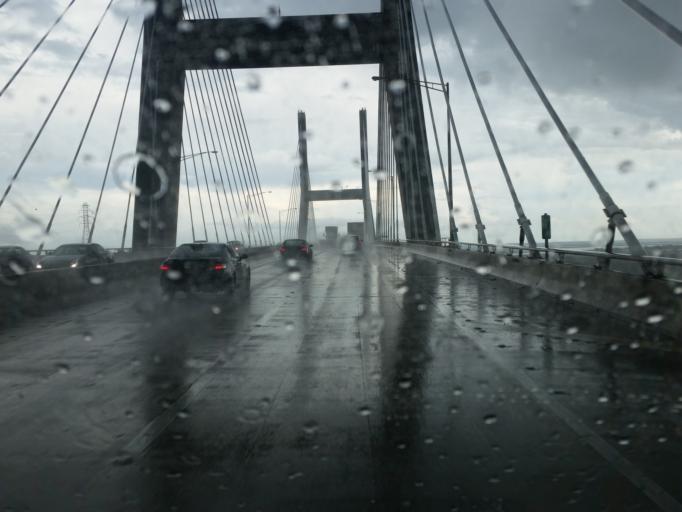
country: US
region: Alabama
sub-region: Mobile County
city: Prichard
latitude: 30.7339
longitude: -88.0448
